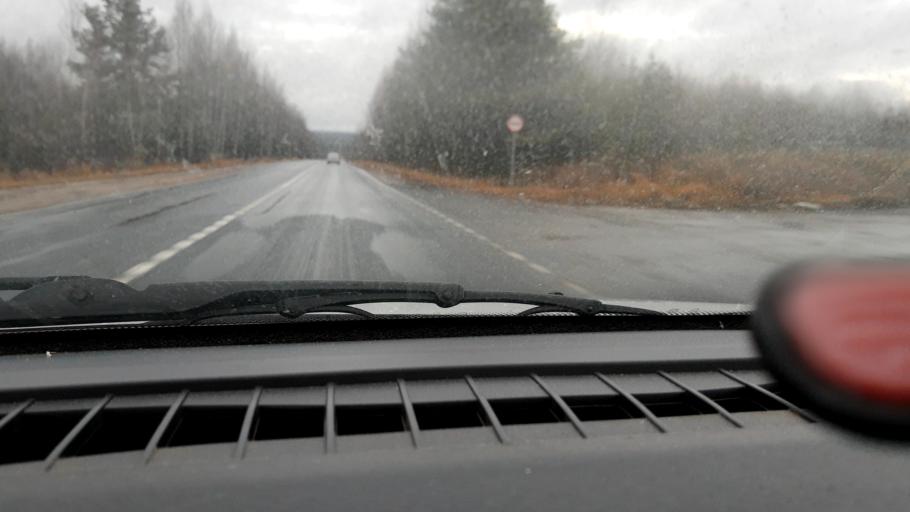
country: RU
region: Nizjnij Novgorod
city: Krasnyye Baki
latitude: 57.1004
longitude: 45.1802
